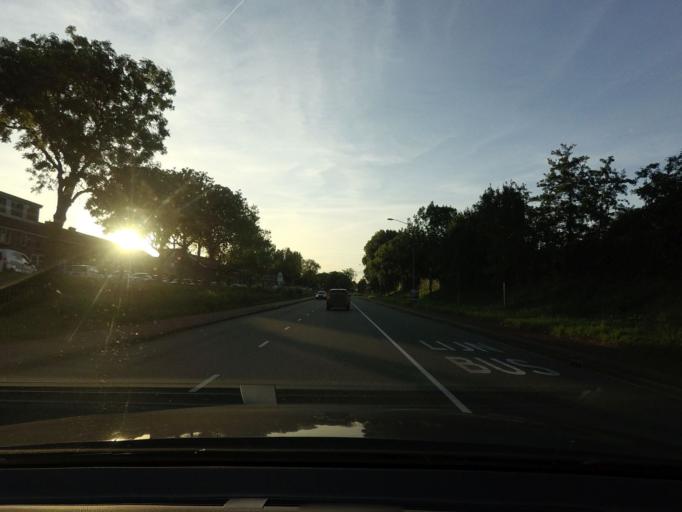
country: NL
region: North Holland
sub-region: Gemeente Alkmaar
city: Alkmaar
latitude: 52.6305
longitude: 4.7602
